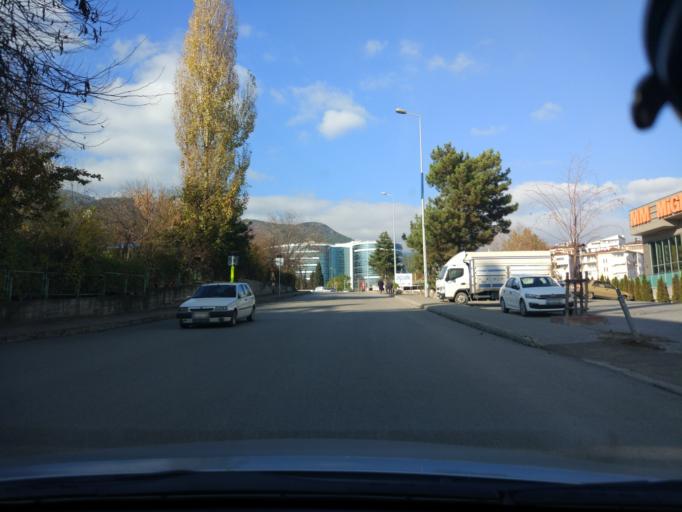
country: TR
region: Karabuk
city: Karabuk
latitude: 41.2055
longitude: 32.6204
